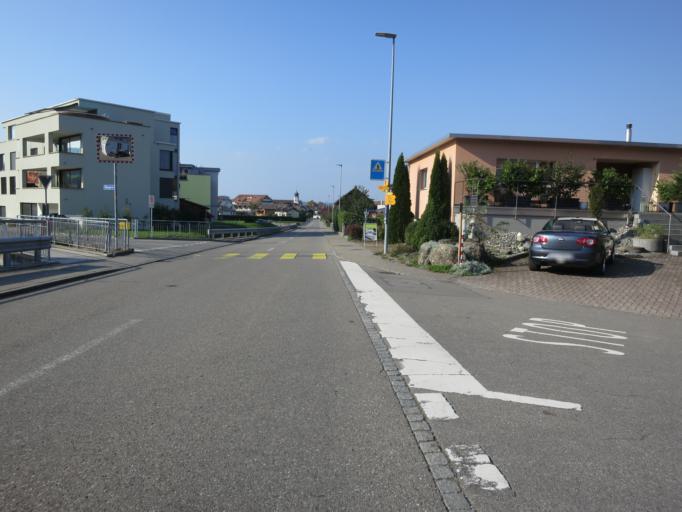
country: CH
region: Schwyz
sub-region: Bezirk March
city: Lachen
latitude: 47.1772
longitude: 8.8779
